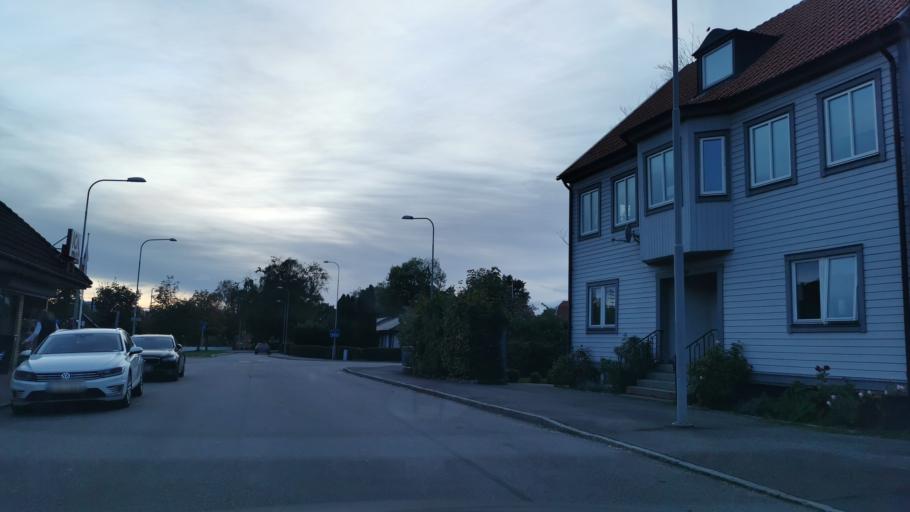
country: SE
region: Vaestra Goetaland
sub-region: Goteborg
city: Eriksbo
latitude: 57.7357
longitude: 12.0459
